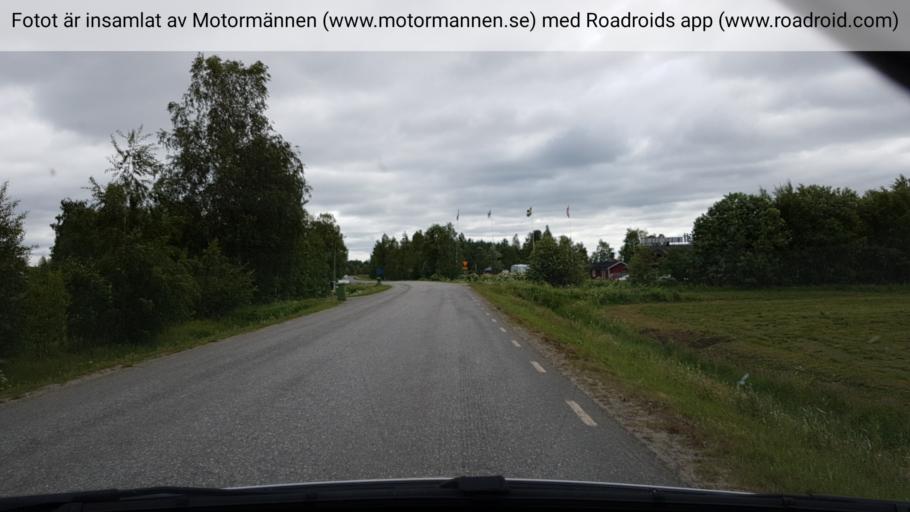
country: SE
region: Vaesterbotten
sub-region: Vannas Kommun
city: Vannasby
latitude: 63.9238
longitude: 19.8569
